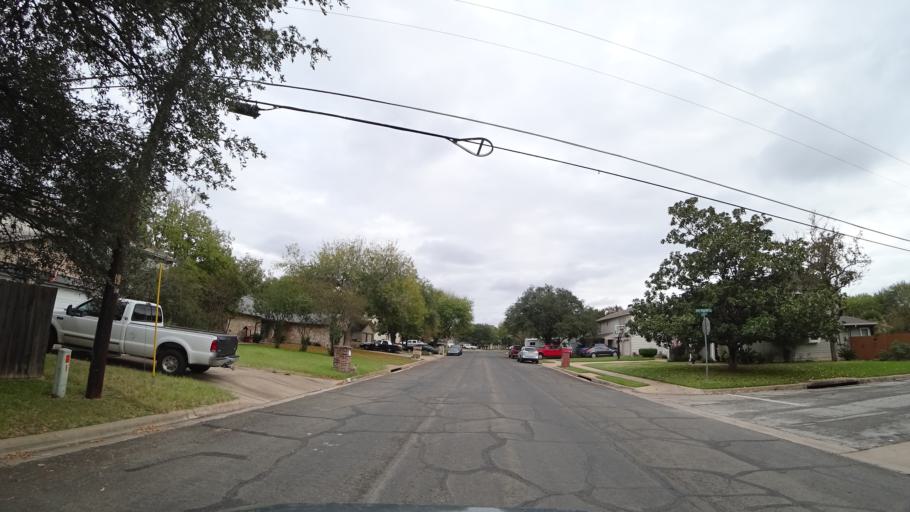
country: US
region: Texas
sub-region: Williamson County
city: Round Rock
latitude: 30.4885
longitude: -97.7022
